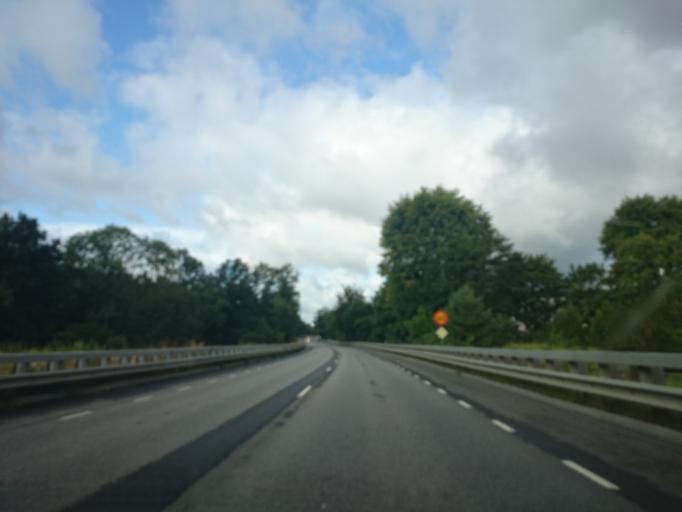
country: SE
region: Skane
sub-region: Kristianstads Kommun
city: Onnestad
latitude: 55.9305
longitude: 13.9804
